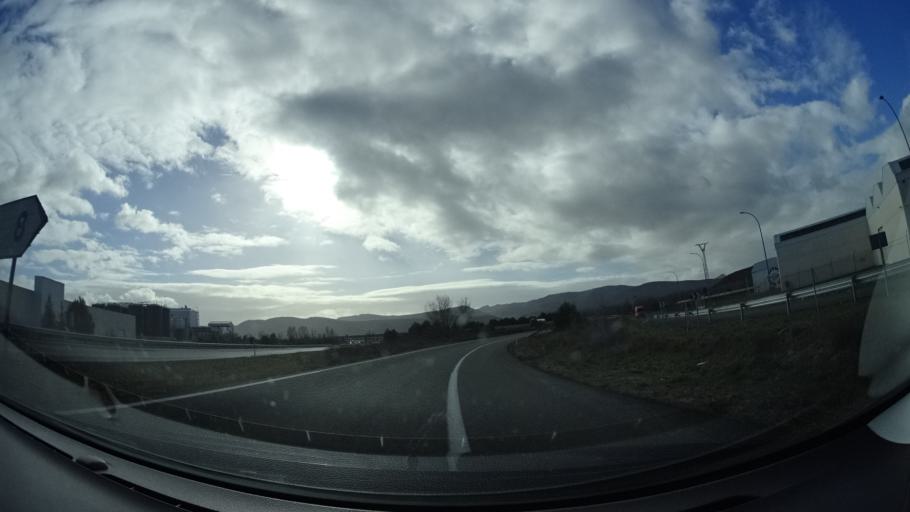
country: ES
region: Basque Country
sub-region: Provincia de Alava
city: Zambrana
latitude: 42.6787
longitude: -2.8892
